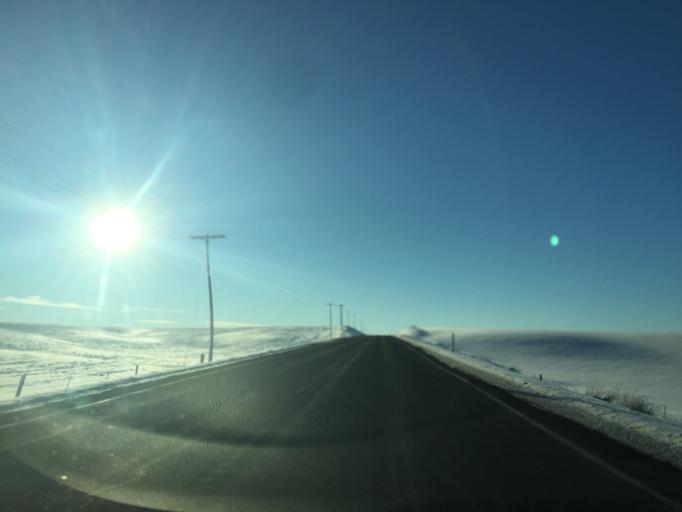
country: US
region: Washington
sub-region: Okanogan County
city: Coulee Dam
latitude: 47.7369
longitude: -118.8503
